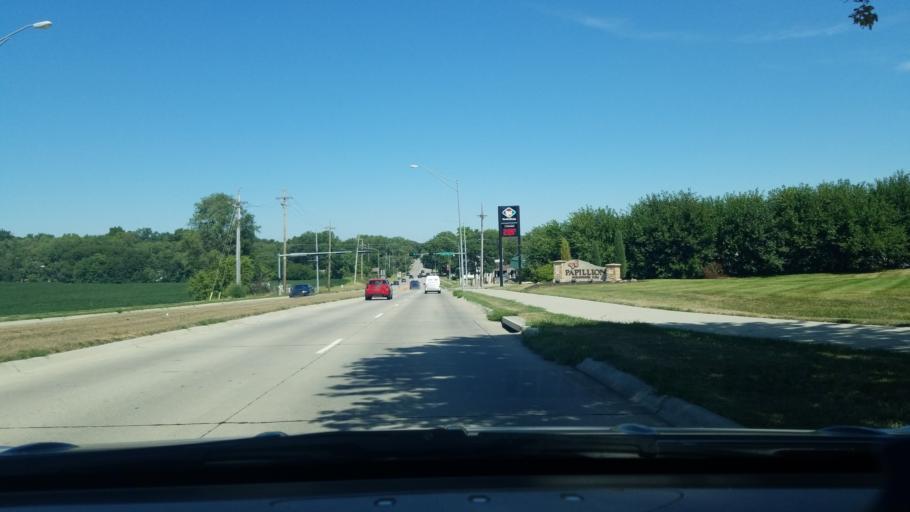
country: US
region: Nebraska
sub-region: Sarpy County
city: Papillion
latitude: 41.1424
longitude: -96.0428
